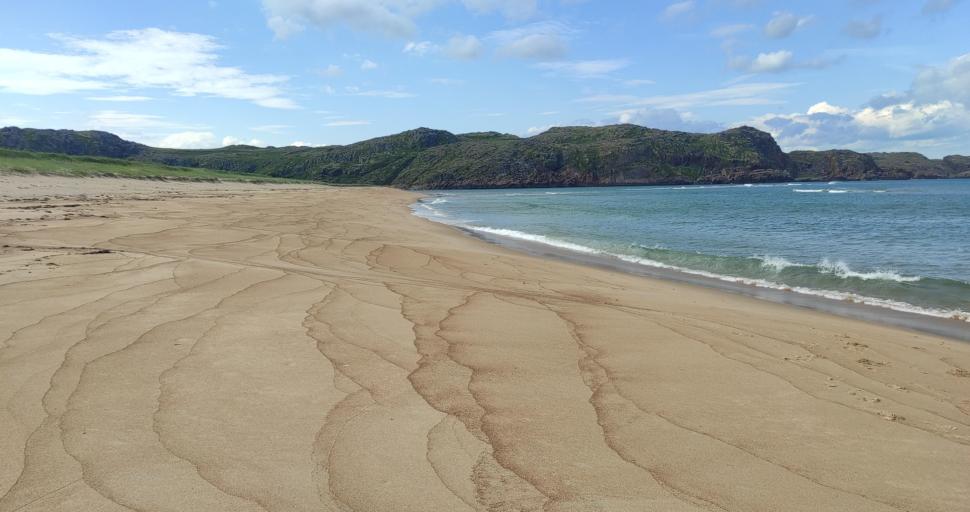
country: RU
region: Murmansk
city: Teriberka
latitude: 69.1789
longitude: 35.7842
